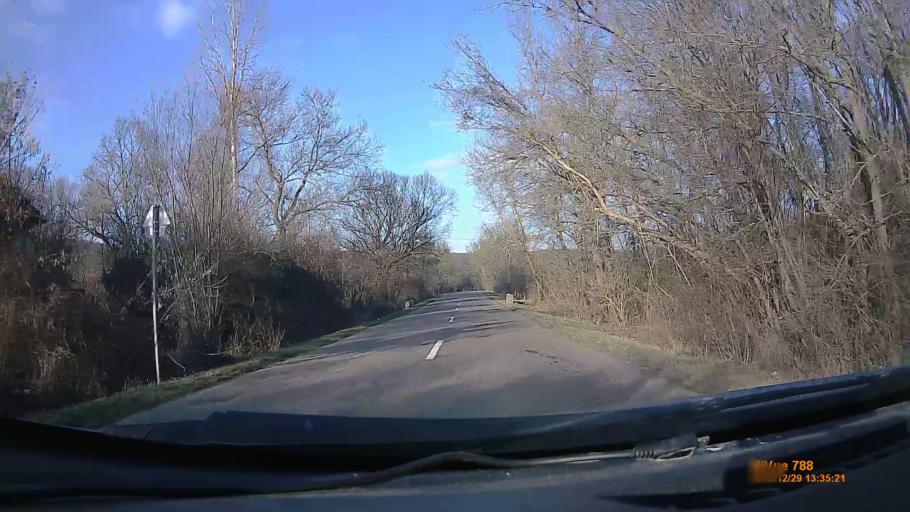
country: HU
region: Heves
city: Sirok
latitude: 47.9085
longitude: 20.1782
